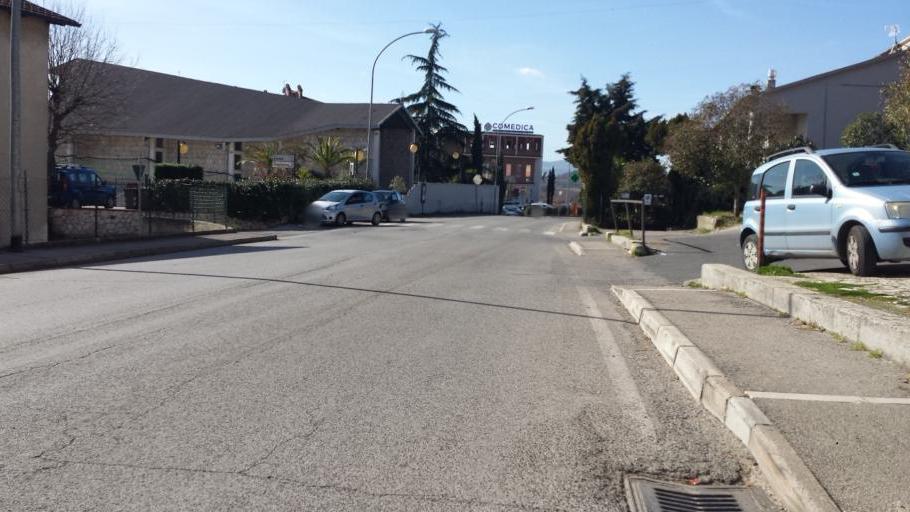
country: IT
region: Umbria
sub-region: Provincia di Terni
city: San Gemini
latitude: 42.5904
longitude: 12.5854
